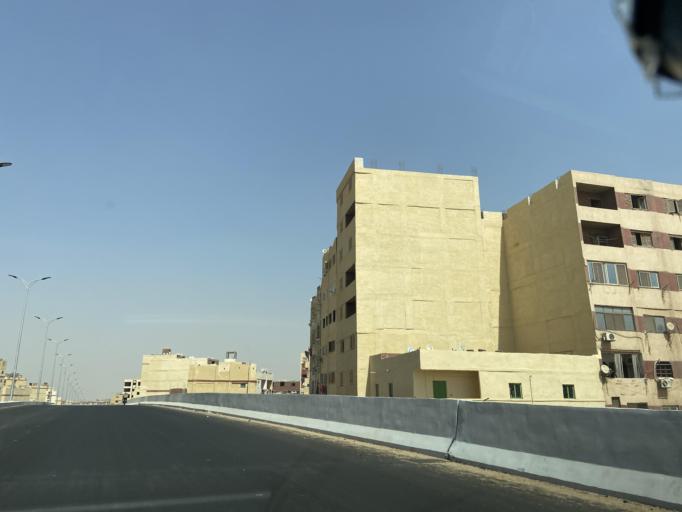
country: EG
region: Muhafazat al Qahirah
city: Cairo
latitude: 30.0629
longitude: 31.3806
